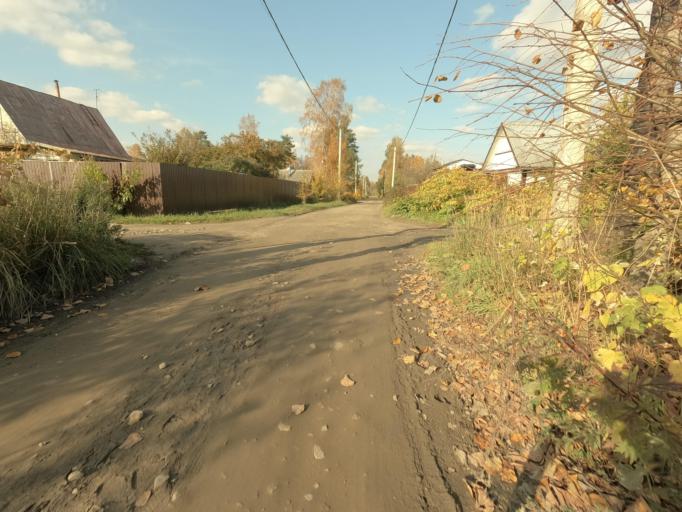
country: RU
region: Leningrad
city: Mga
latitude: 59.7634
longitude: 31.1168
